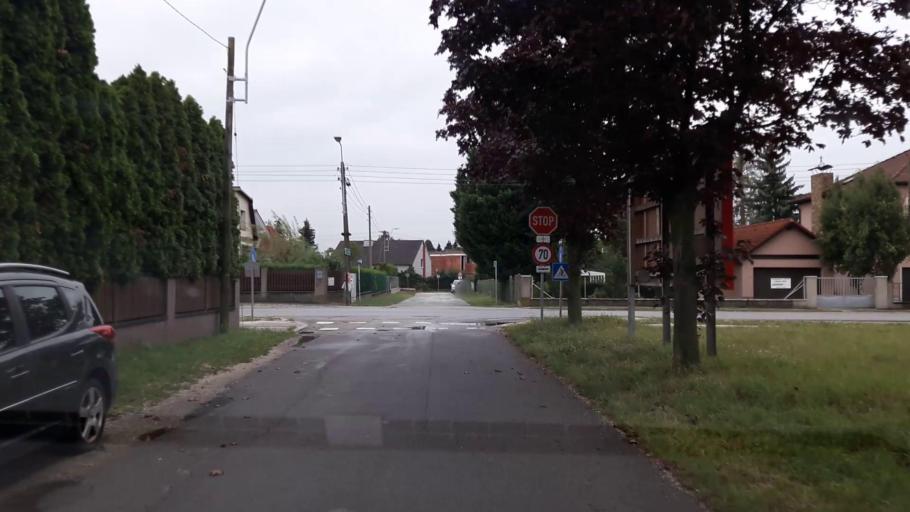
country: AT
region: Lower Austria
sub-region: Politischer Bezirk Ganserndorf
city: Strasshof an der Nordbahn
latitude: 48.3211
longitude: 16.6573
